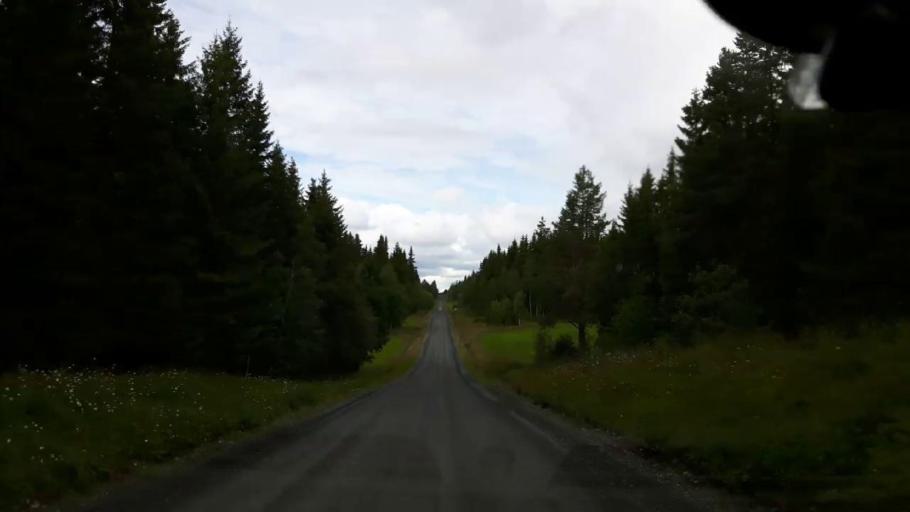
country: SE
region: Jaemtland
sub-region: Krokoms Kommun
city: Valla
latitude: 63.5036
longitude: 13.9598
